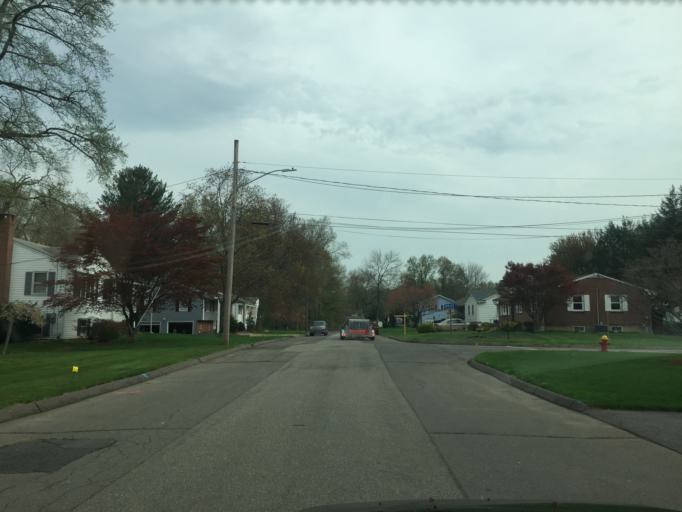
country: US
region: Connecticut
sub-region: Hartford County
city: Newington
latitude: 41.6898
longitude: -72.7412
